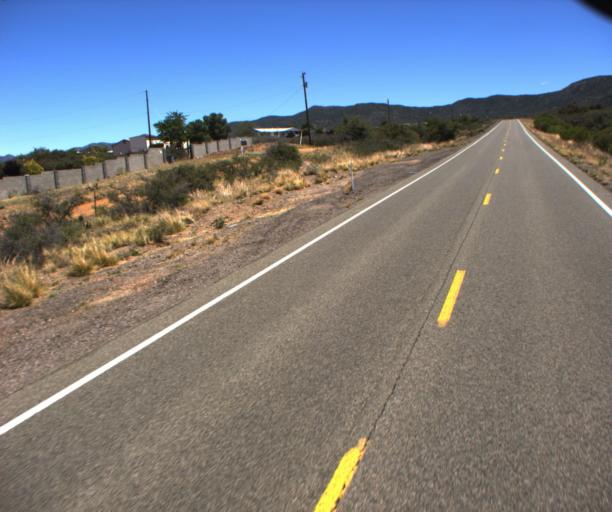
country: US
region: Arizona
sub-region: Yavapai County
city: Prescott
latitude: 34.4175
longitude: -112.5987
